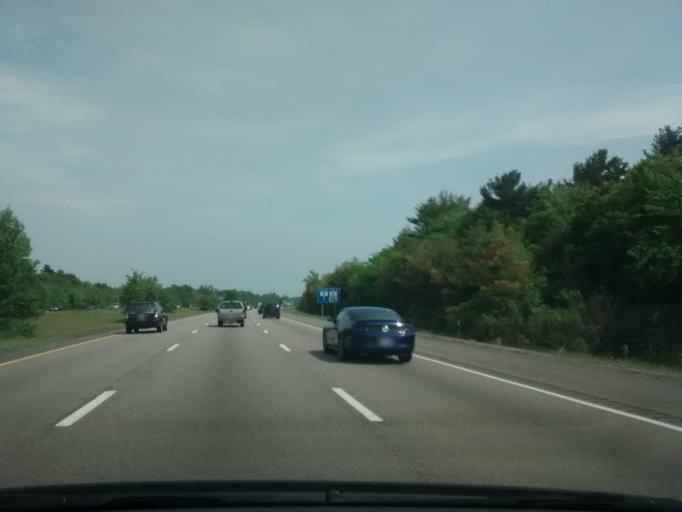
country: US
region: Massachusetts
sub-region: Bristol County
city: Mansfield Center
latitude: 42.0232
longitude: -71.2502
